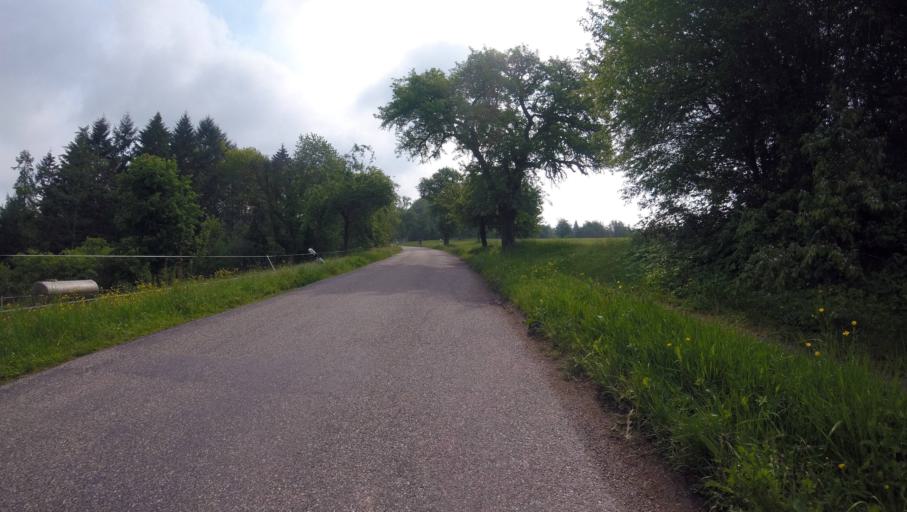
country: DE
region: Baden-Wuerttemberg
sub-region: Regierungsbezirk Stuttgart
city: Althutte
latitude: 48.9339
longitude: 9.5416
